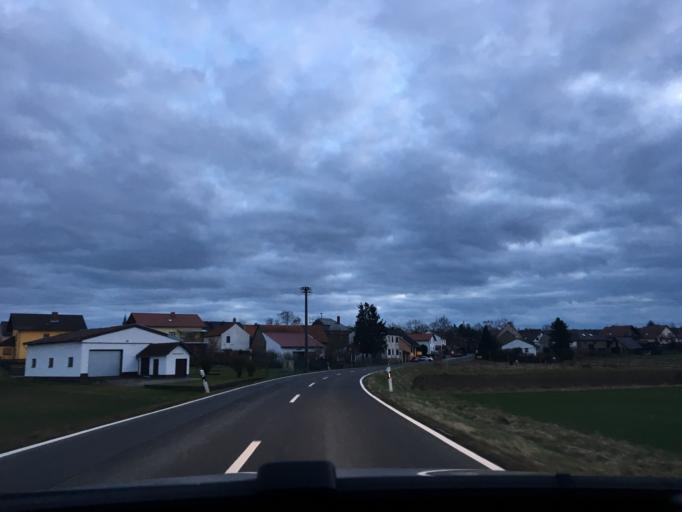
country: DE
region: Rheinland-Pfalz
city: Bechenheim
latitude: 49.7309
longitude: 8.0031
